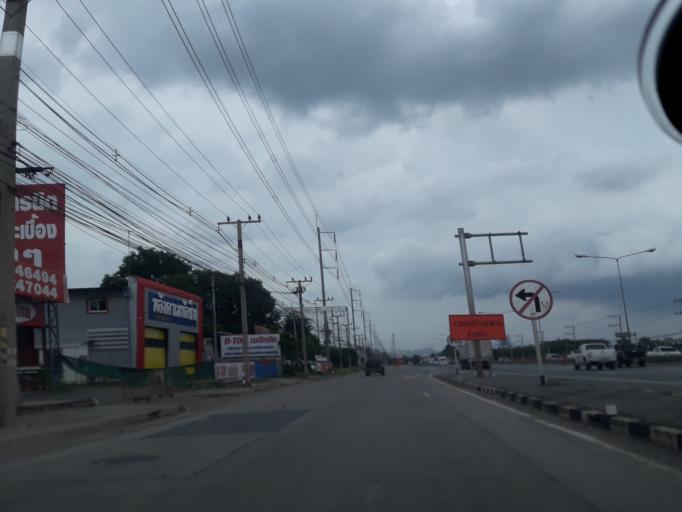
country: TH
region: Sara Buri
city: Kaeng Khoi
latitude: 14.5634
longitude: 100.9754
